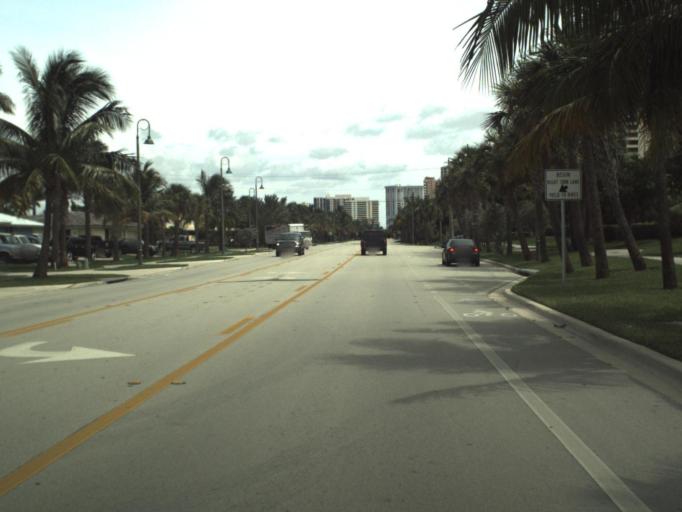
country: US
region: Florida
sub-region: Palm Beach County
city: Palm Beach Shores
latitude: 26.7931
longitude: -80.0345
